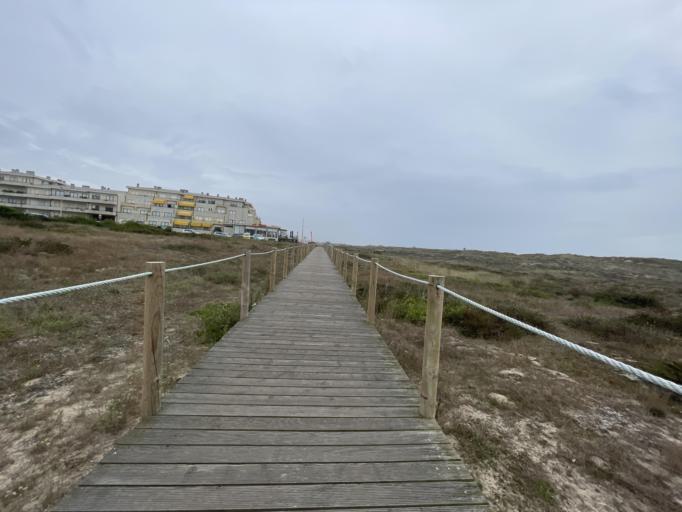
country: PT
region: Porto
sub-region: Vila do Conde
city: Vila do Conde
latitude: 41.3389
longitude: -8.7410
